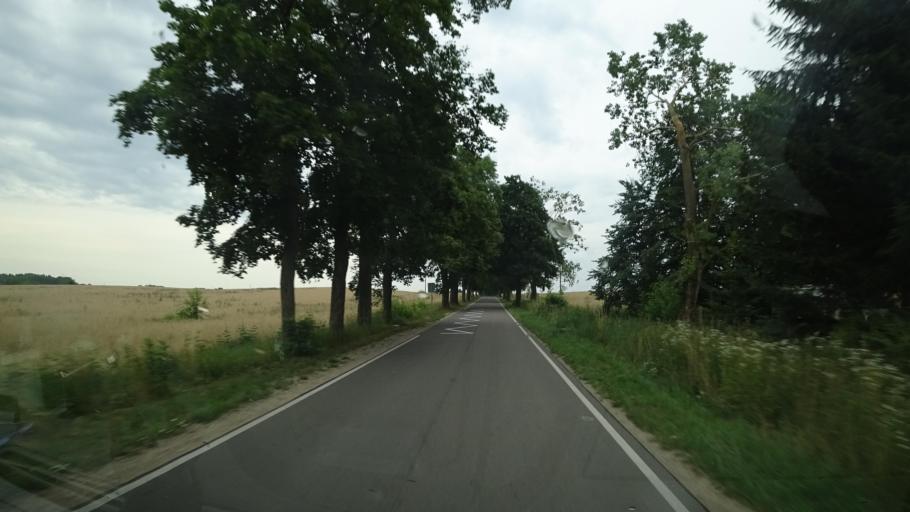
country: PL
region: Warmian-Masurian Voivodeship
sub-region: Powiat mragowski
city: Mikolajki
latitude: 53.8623
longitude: 21.6028
